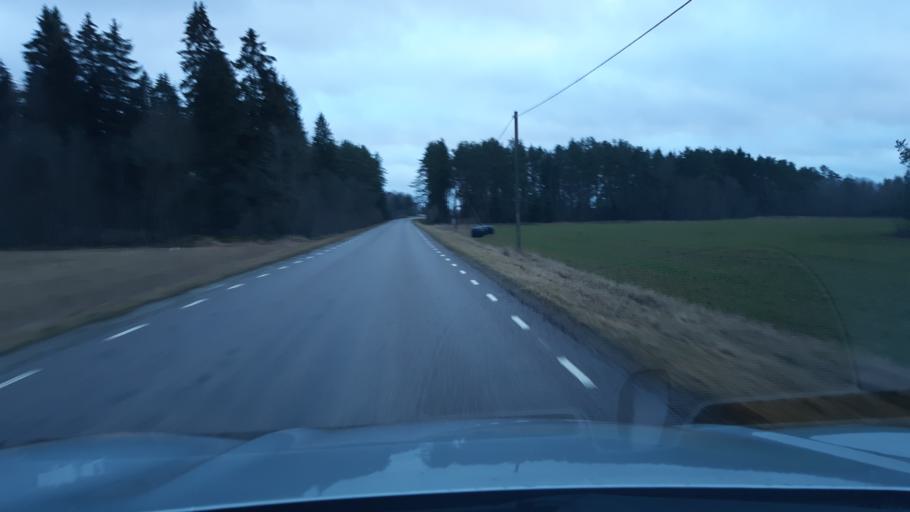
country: EE
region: Raplamaa
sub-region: Kohila vald
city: Kohila
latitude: 59.0755
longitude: 24.6799
